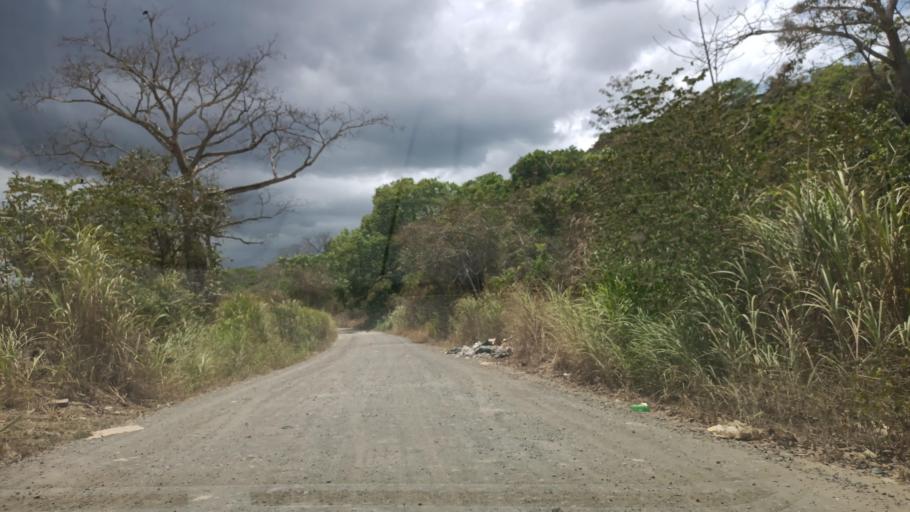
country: PA
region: Panama
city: Las Cumbres
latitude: 9.0597
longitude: -79.5671
